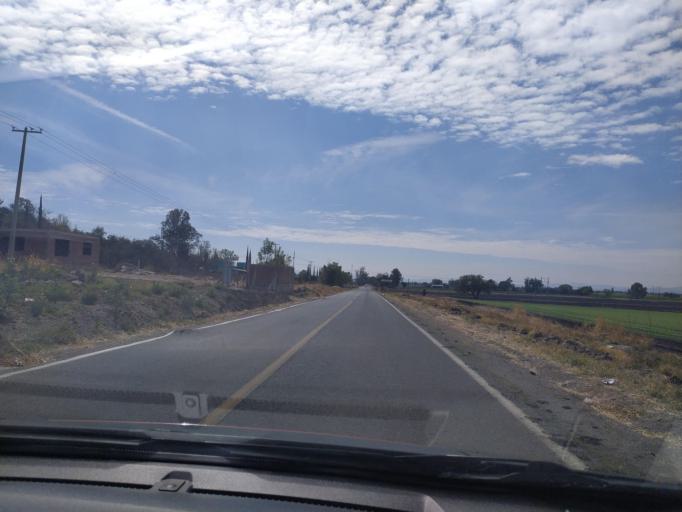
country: MX
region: Guanajuato
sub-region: San Francisco del Rincon
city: San Ignacio de Hidalgo
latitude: 20.8654
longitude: -101.8605
